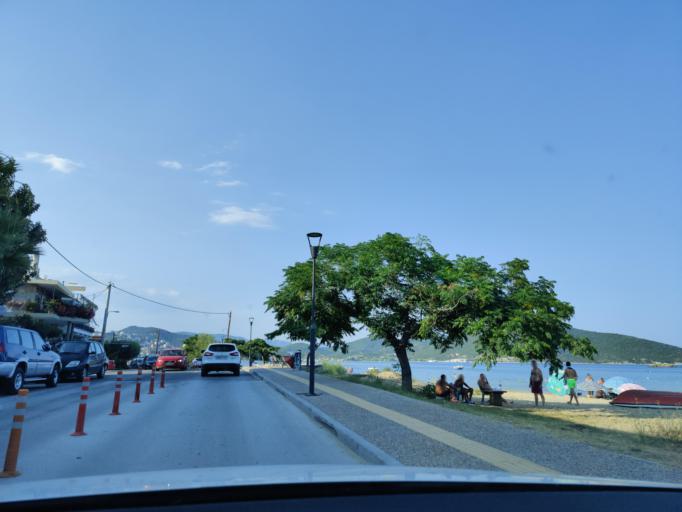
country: GR
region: East Macedonia and Thrace
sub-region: Nomos Kavalas
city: Nea Peramos
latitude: 40.8349
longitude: 24.3052
